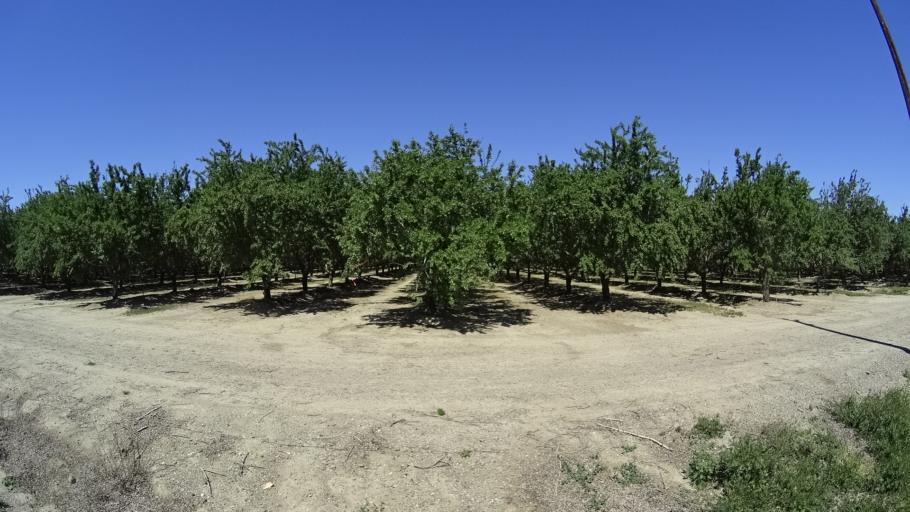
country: US
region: California
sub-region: Glenn County
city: Orland
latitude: 39.7323
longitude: -122.1359
